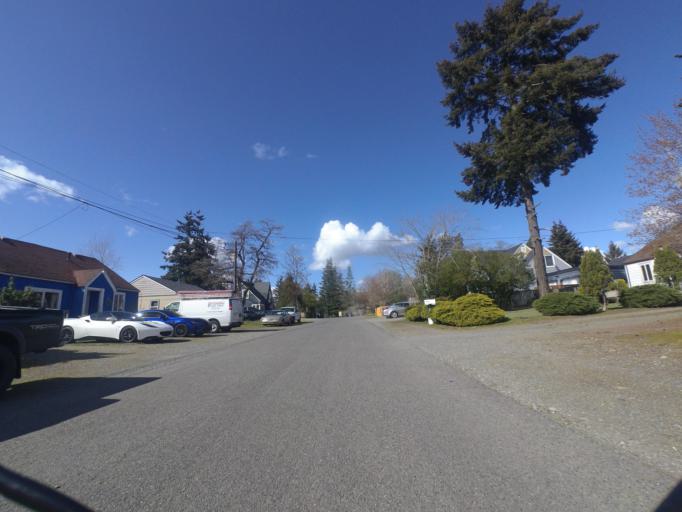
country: US
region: Washington
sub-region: Pierce County
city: Lakewood
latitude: 47.1629
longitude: -122.4981
